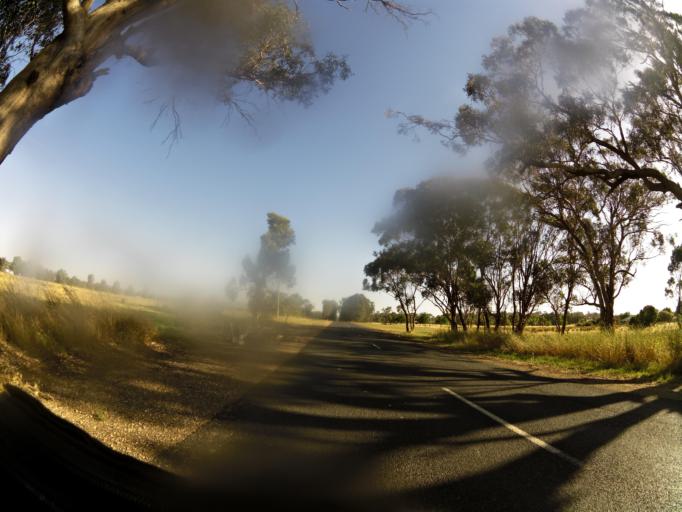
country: AU
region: Victoria
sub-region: Murrindindi
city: Kinglake West
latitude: -36.9859
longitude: 145.1116
